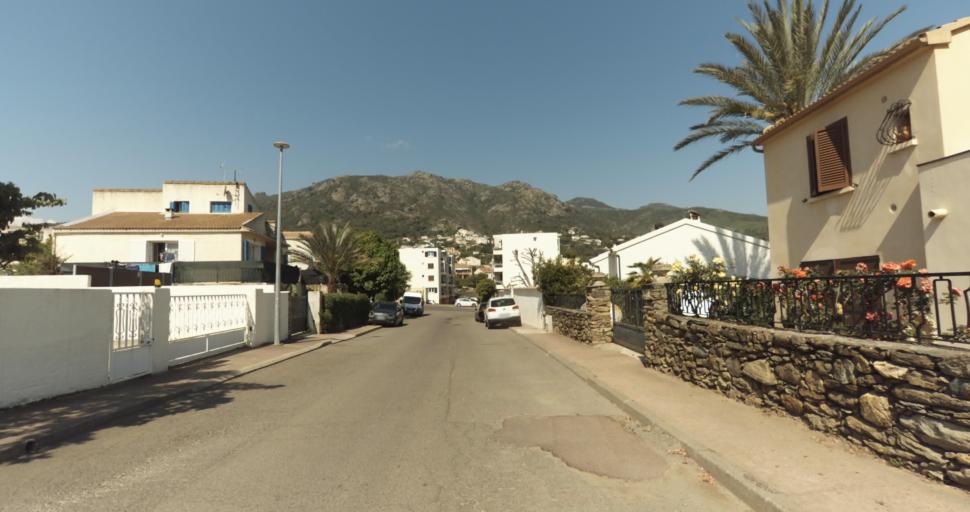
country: FR
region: Corsica
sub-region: Departement de la Haute-Corse
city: Biguglia
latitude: 42.6261
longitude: 9.4325
